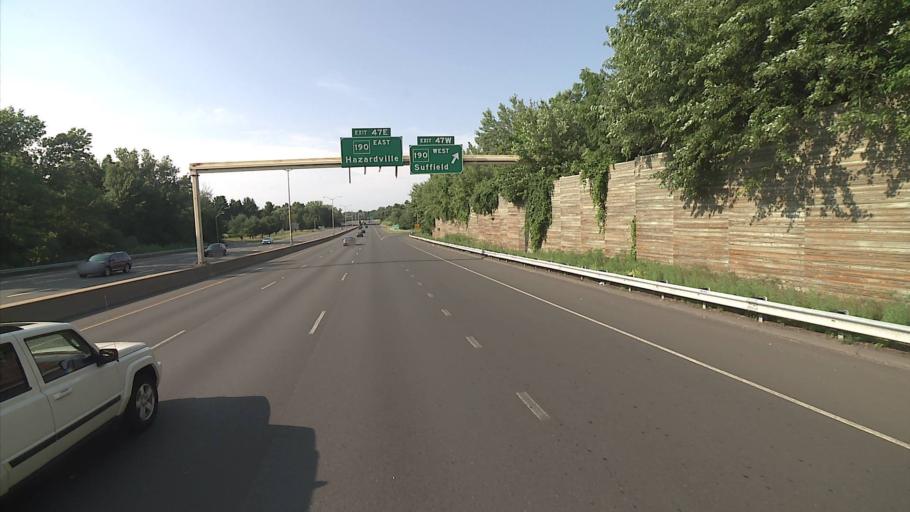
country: US
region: Connecticut
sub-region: Hartford County
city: Thompsonville
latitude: 41.9946
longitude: -72.5868
